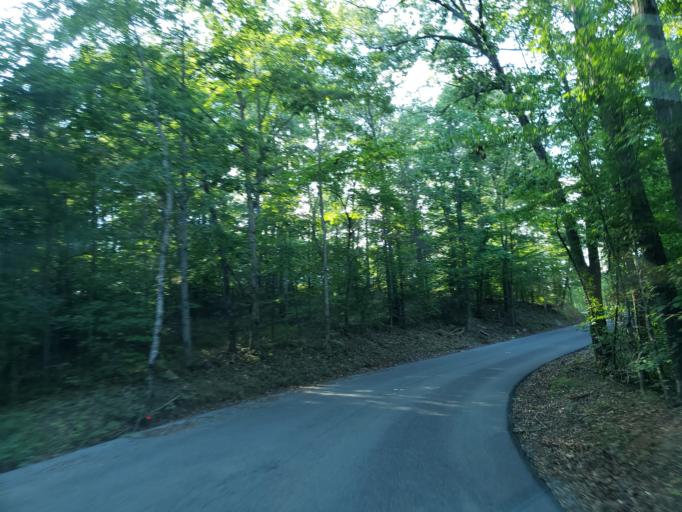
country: US
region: Georgia
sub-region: Paulding County
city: Dallas
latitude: 34.0170
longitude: -84.9015
